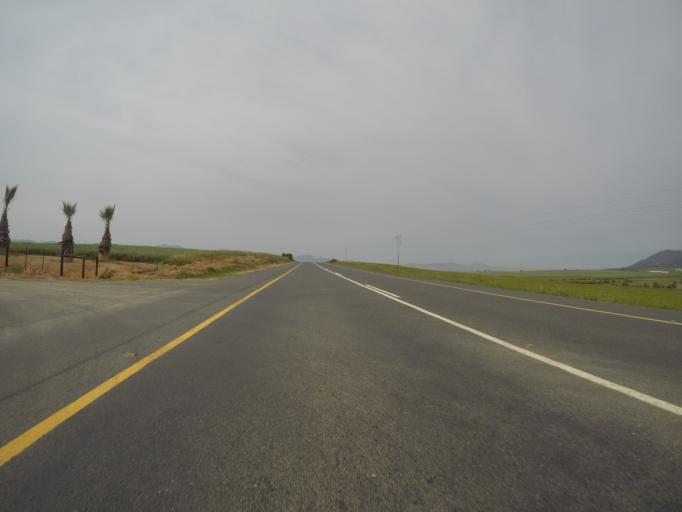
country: ZA
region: Western Cape
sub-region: West Coast District Municipality
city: Malmesbury
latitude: -33.5492
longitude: 18.8674
